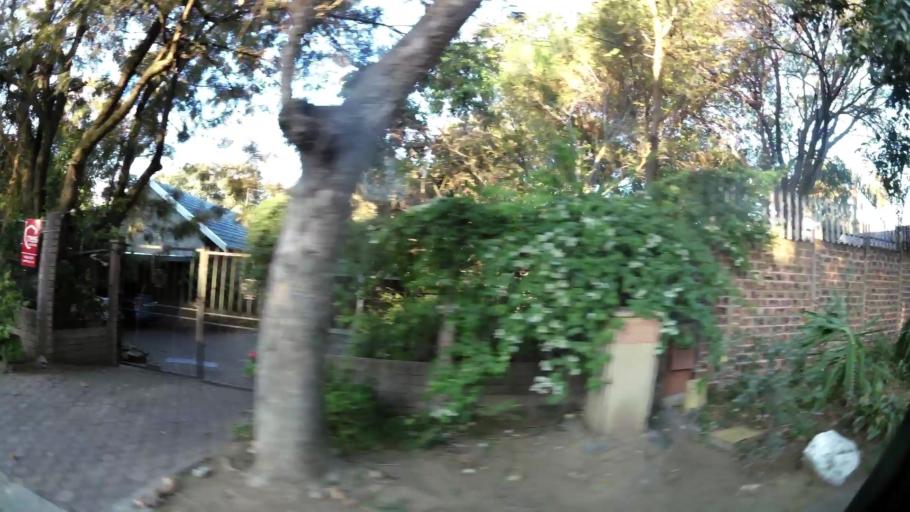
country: ZA
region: Gauteng
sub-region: City of Johannesburg Metropolitan Municipality
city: Diepsloot
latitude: -26.0376
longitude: 27.9769
